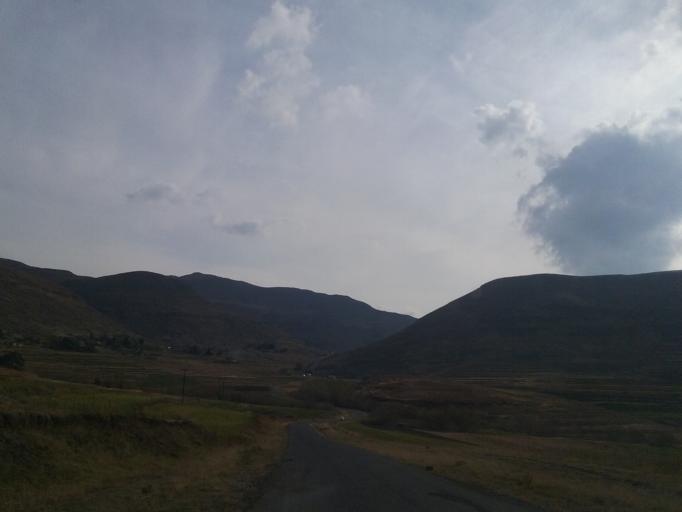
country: LS
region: Quthing
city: Quthing
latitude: -30.1898
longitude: 28.0873
